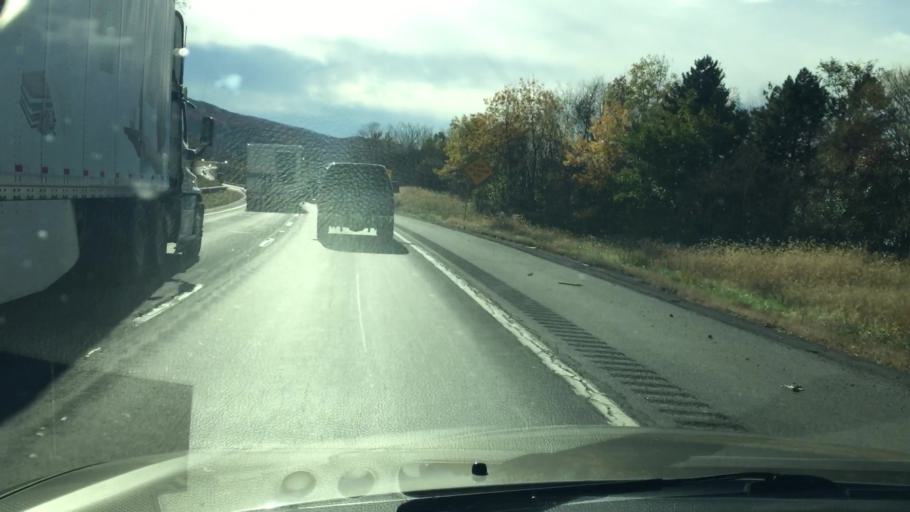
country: US
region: Pennsylvania
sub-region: Luzerne County
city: Ashley
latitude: 41.2115
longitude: -75.8964
